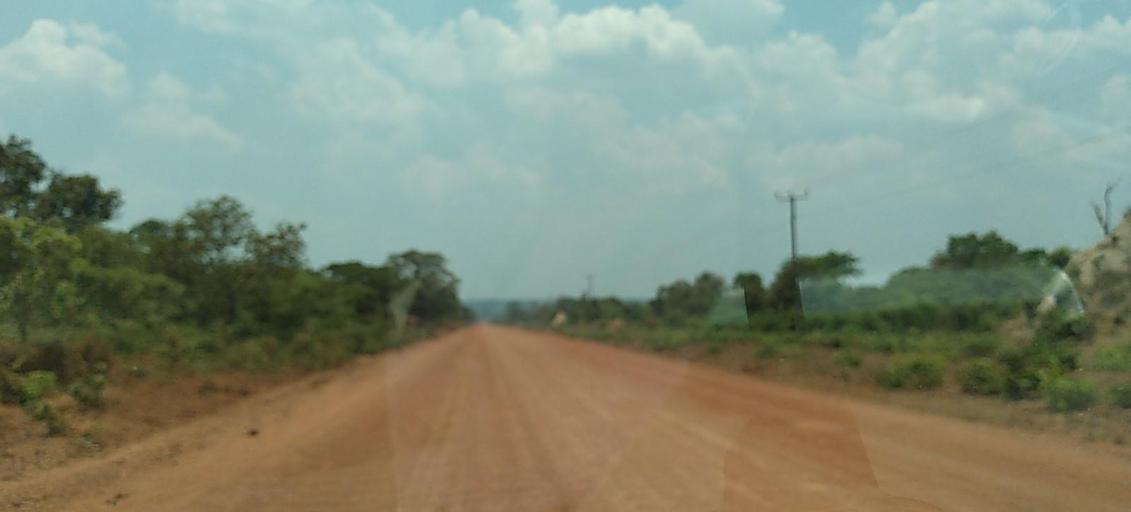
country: ZM
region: Copperbelt
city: Chingola
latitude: -12.8831
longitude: 27.5879
